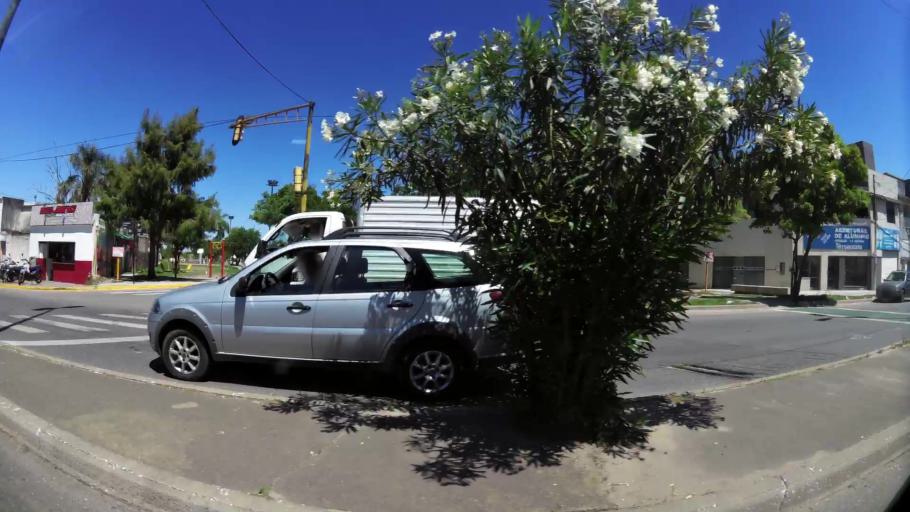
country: AR
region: Santa Fe
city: Santa Fe de la Vera Cruz
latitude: -31.6203
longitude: -60.7055
